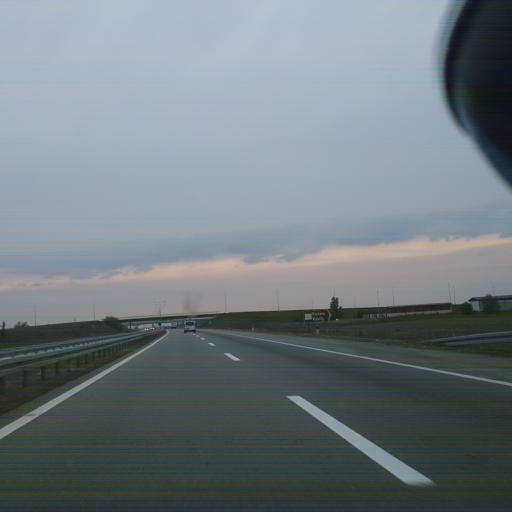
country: RS
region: Autonomna Pokrajina Vojvodina
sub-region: Juznobacki Okrug
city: Kovilj
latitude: 45.2383
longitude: 20.0413
